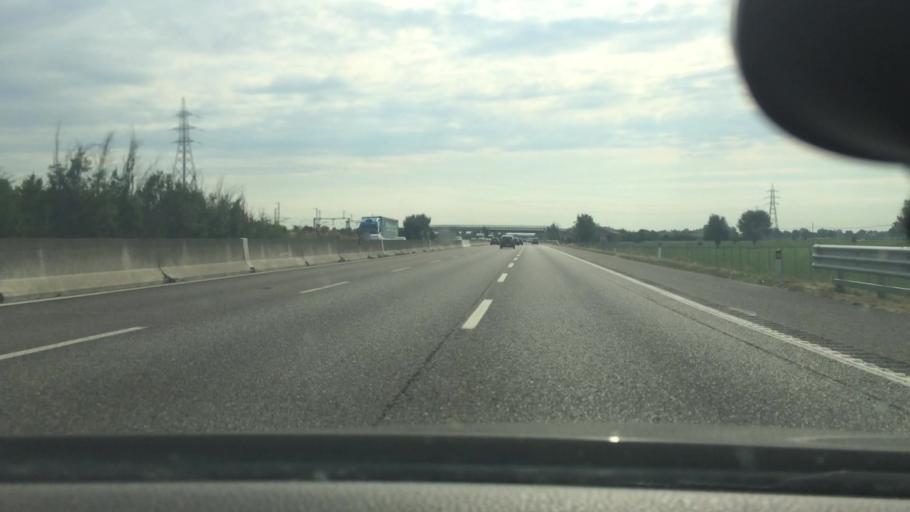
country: IT
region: Emilia-Romagna
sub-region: Provincia di Parma
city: Soragna
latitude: 44.8839
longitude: 10.1267
